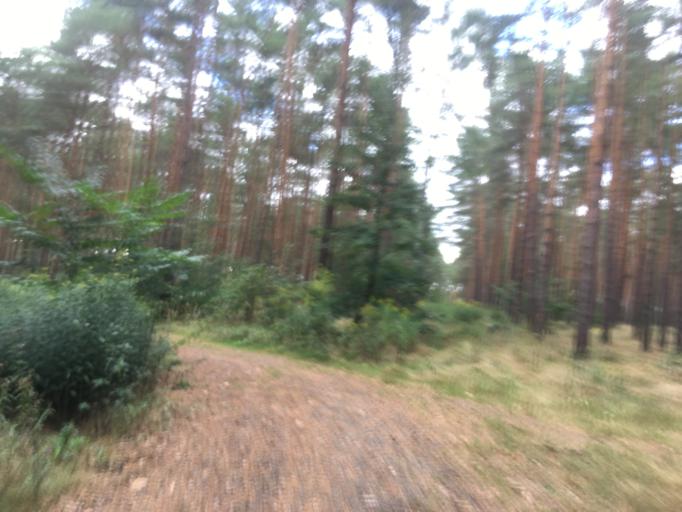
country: DE
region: Brandenburg
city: Wildau
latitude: 52.3185
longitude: 13.7002
